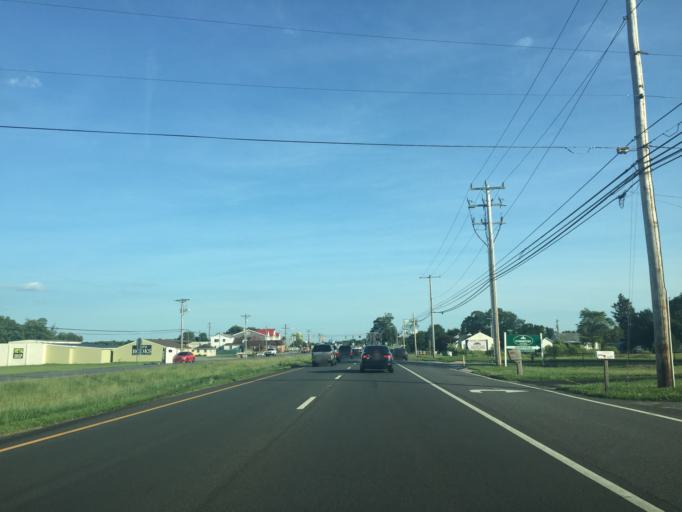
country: US
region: Delaware
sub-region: Kent County
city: Smyrna
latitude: 39.2717
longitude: -75.5897
